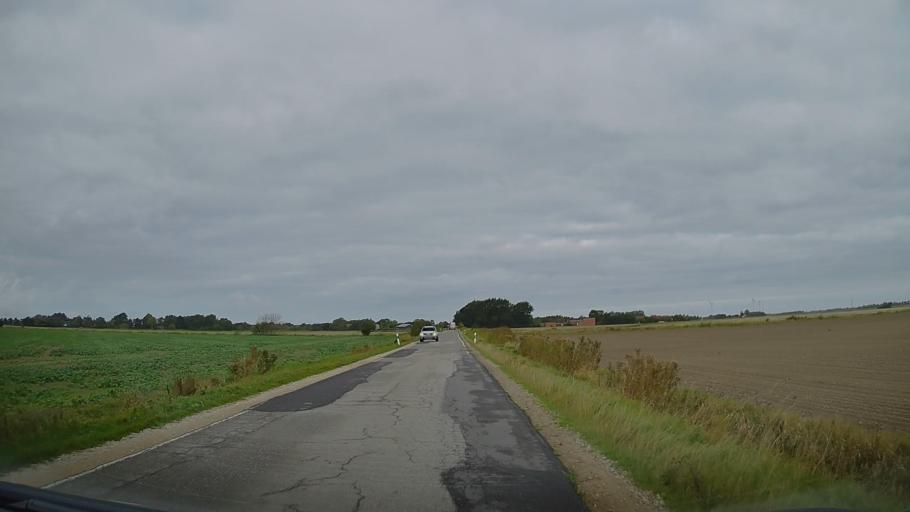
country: DE
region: Schleswig-Holstein
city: Emmelsbull-Horsbull
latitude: 54.8040
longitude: 8.7113
